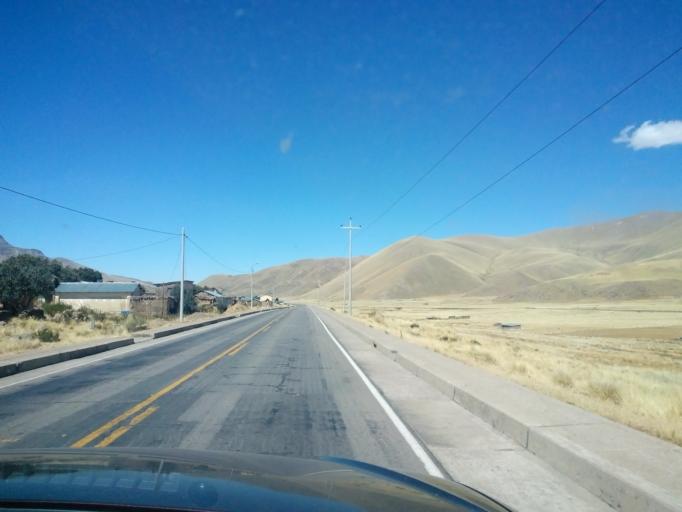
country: PE
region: Puno
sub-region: Provincia de Melgar
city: Santa Rosa
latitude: -14.5103
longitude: -70.9240
